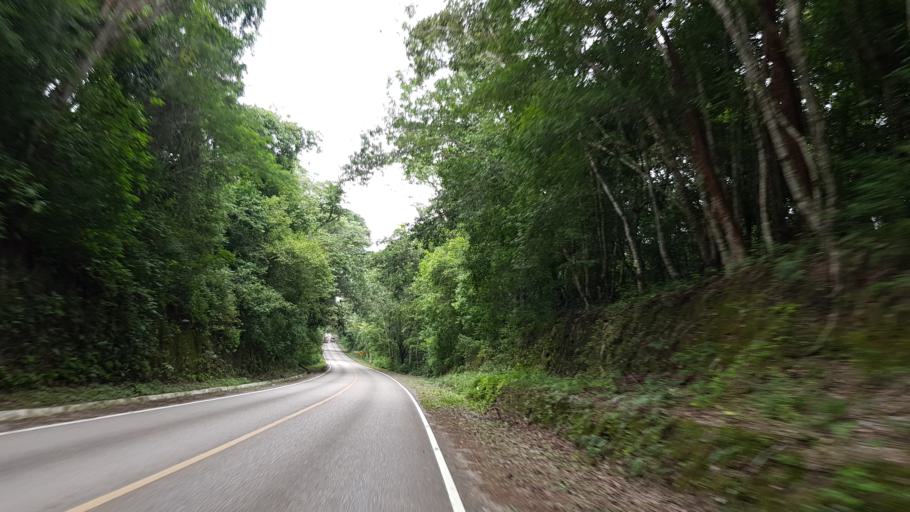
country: GT
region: Peten
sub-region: Municipio de San Jose
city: San Jose
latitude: 17.2179
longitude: -89.6116
